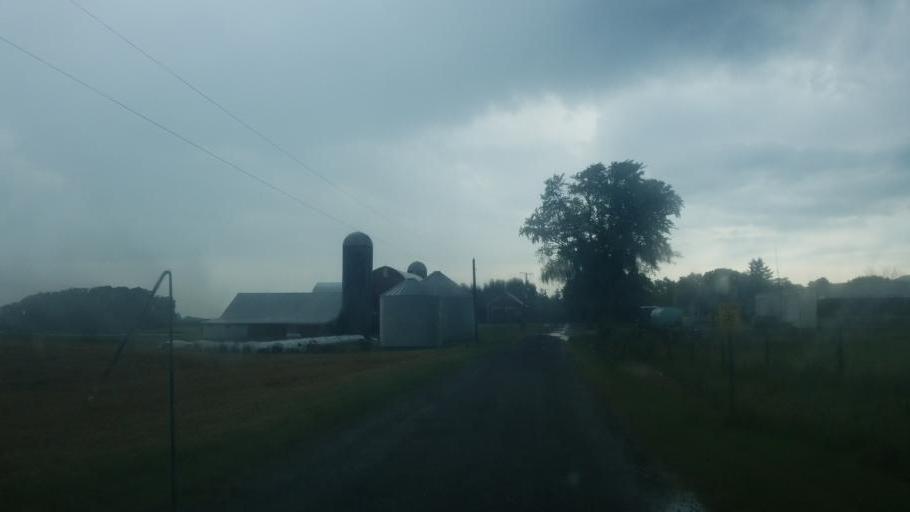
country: US
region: Indiana
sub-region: DeKalb County
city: Butler
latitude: 41.4623
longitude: -84.8184
